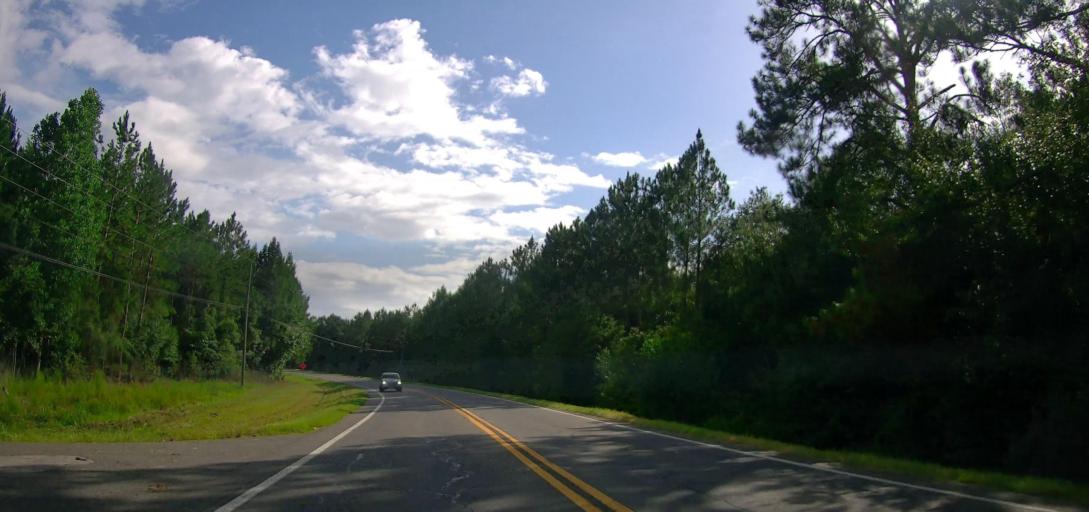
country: US
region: Georgia
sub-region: Coffee County
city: Douglas
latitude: 31.4591
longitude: -82.8879
